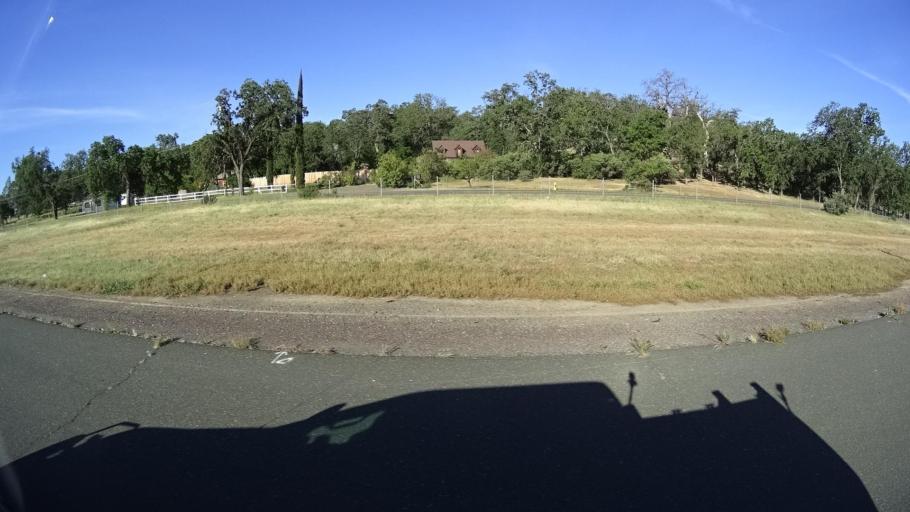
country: US
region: California
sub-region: Lake County
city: Lakeport
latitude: 39.0238
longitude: -122.9176
